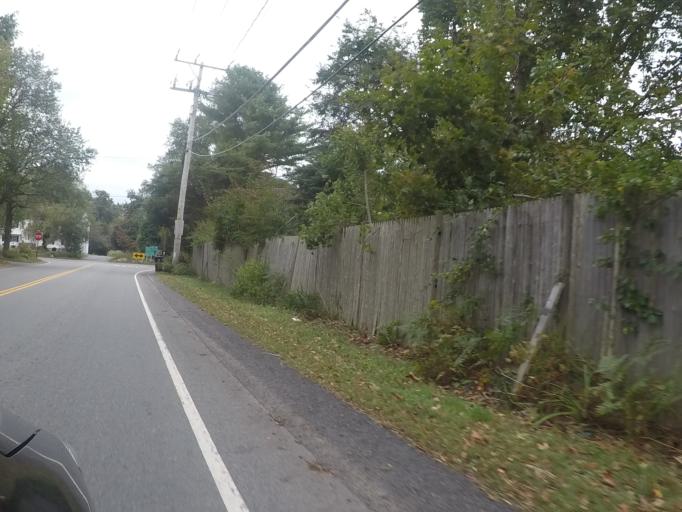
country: US
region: Massachusetts
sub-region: Bristol County
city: Smith Mills
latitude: 41.5848
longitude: -70.9996
